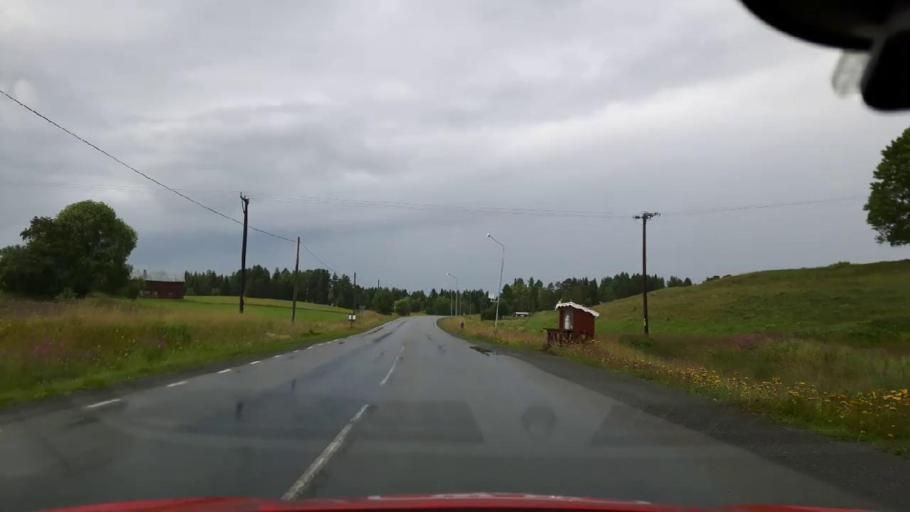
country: SE
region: Jaemtland
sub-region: Krokoms Kommun
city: Krokom
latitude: 63.3252
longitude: 14.2975
